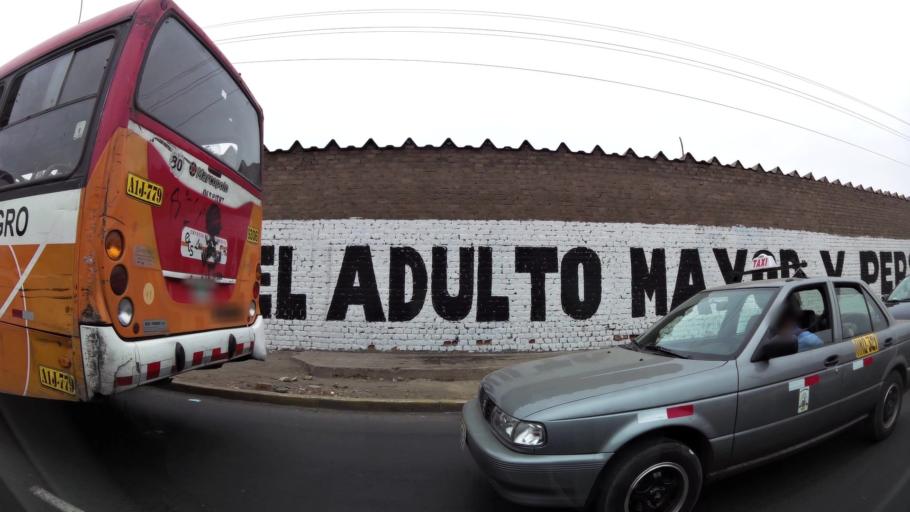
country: PE
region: Callao
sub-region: Callao
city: Callao
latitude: -12.0499
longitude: -77.1062
